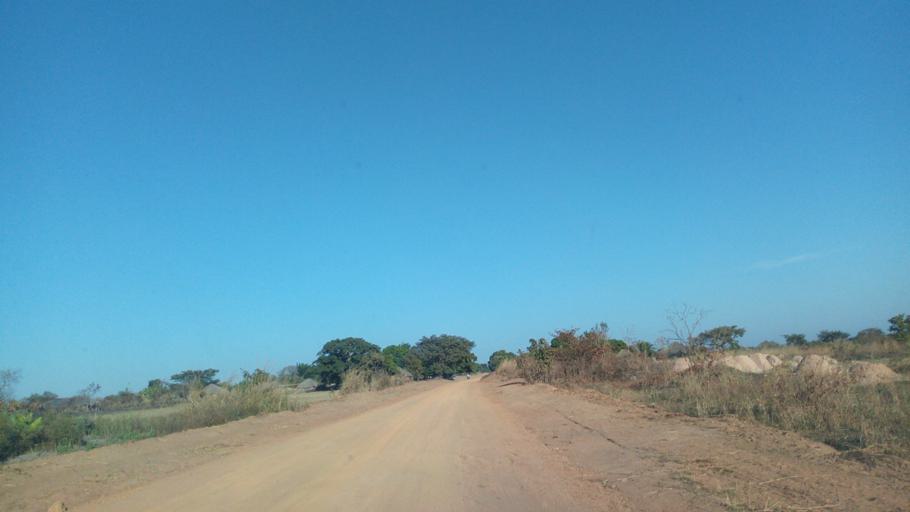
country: ZM
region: Luapula
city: Mwense
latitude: -10.4551
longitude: 28.5429
